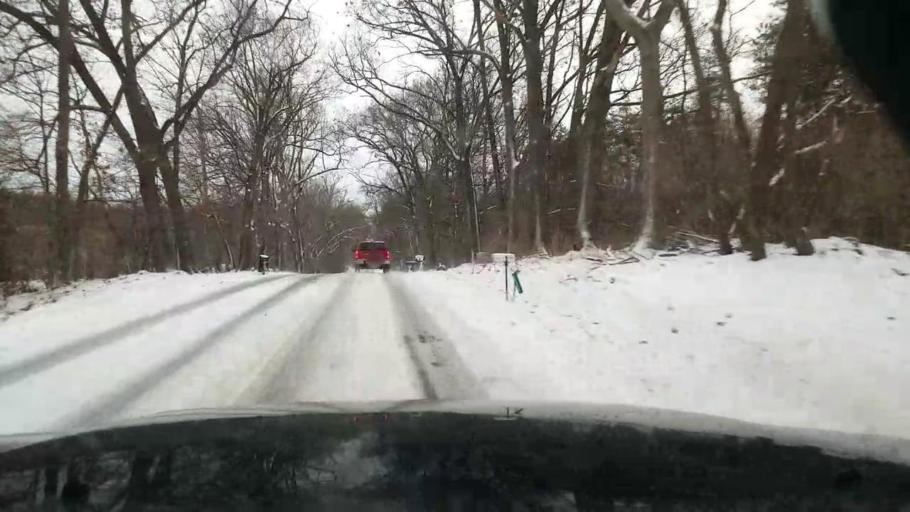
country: US
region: Michigan
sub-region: Jackson County
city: Spring Arbor
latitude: 42.1859
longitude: -84.5009
